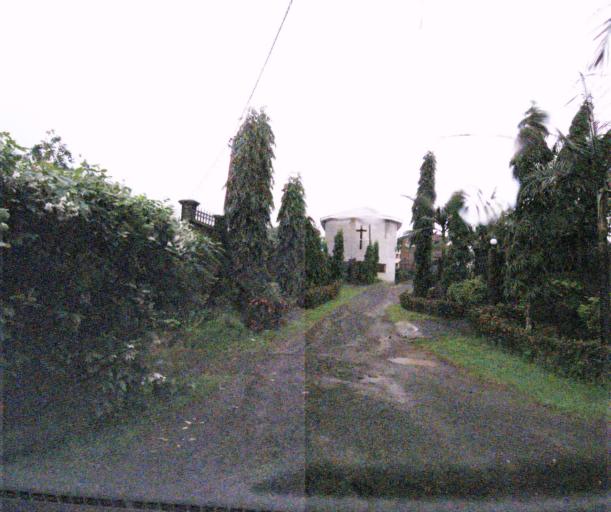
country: CM
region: South-West Province
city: Limbe
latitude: 4.0187
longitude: 9.1881
